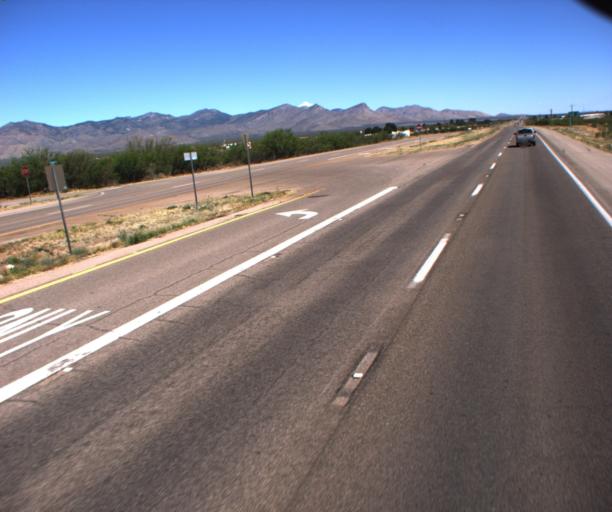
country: US
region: Arizona
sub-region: Cochise County
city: Huachuca City
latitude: 31.6974
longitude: -110.3501
